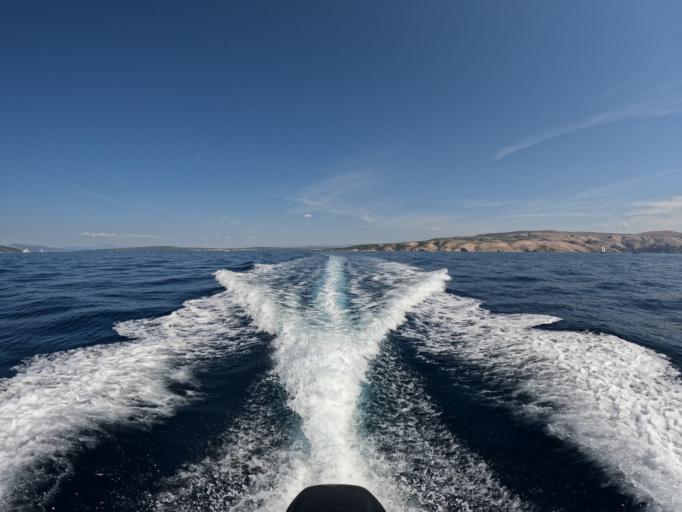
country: HR
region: Primorsko-Goranska
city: Punat
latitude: 44.9380
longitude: 14.6159
